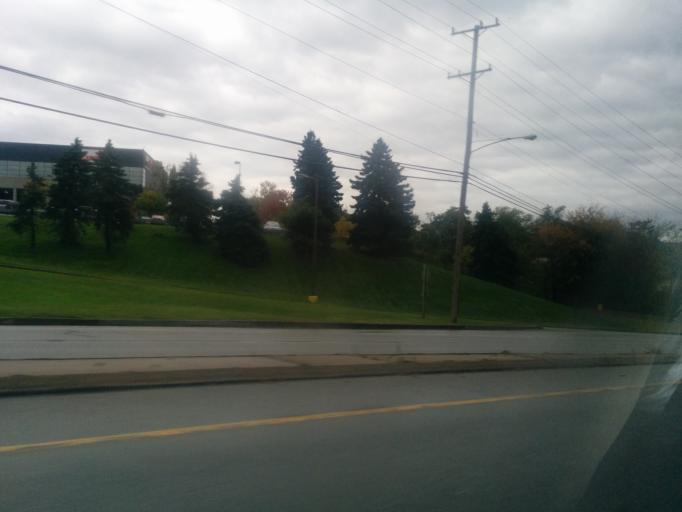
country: US
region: Pennsylvania
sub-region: Allegheny County
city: Monroeville
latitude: 40.4341
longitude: -79.7949
